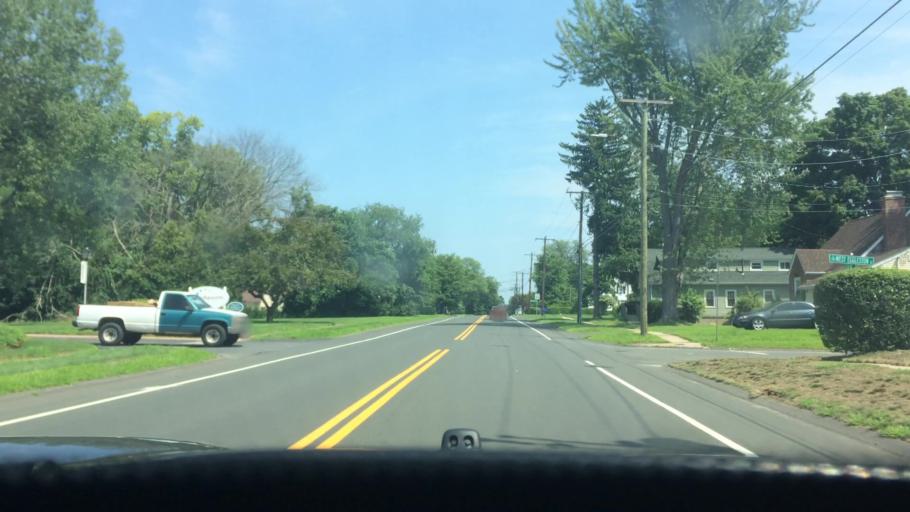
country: US
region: Connecticut
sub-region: Hartford County
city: Blue Hills
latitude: 41.8230
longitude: -72.7043
